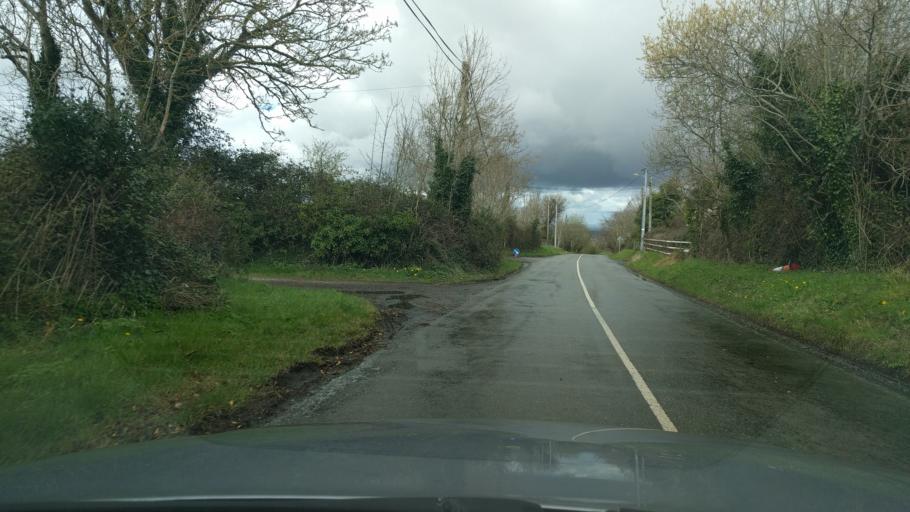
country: IE
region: Leinster
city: Oldbawn
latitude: 53.2483
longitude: -6.3606
